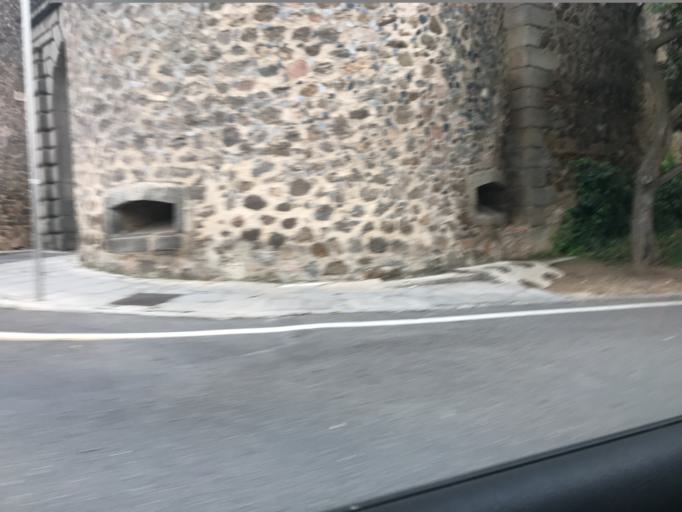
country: ES
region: Castille-La Mancha
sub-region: Province of Toledo
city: Toledo
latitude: 39.8628
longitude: -4.0253
